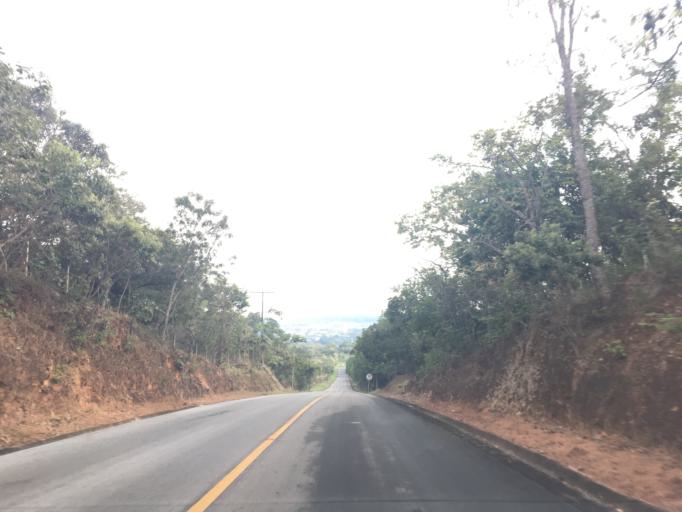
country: BR
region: Federal District
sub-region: Brasilia
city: Brasilia
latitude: -15.8021
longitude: -47.7996
